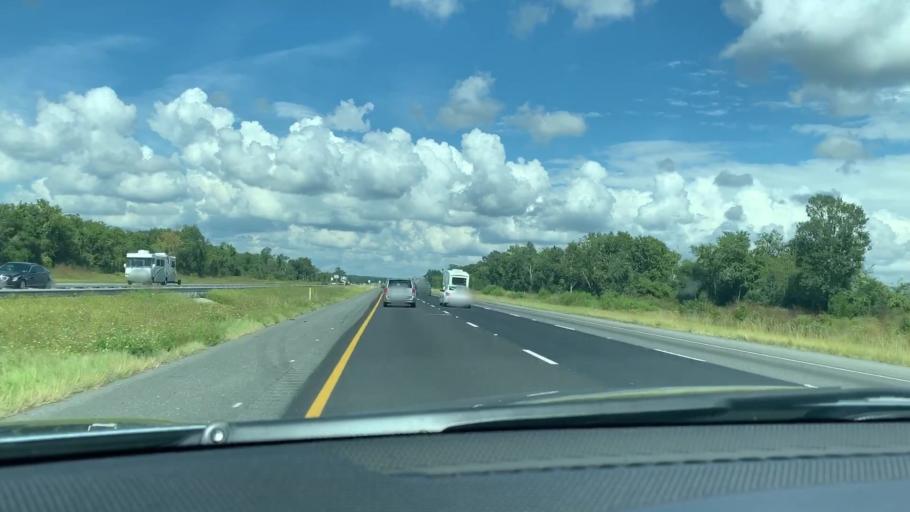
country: US
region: Georgia
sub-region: Camden County
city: Woodbine
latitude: 31.0203
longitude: -81.6578
